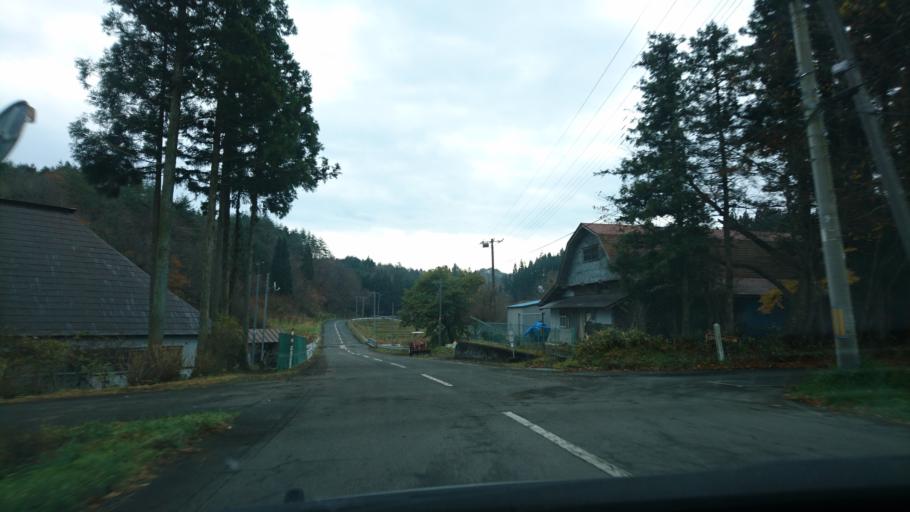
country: JP
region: Iwate
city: Ichinoseki
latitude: 38.9332
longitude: 140.9211
